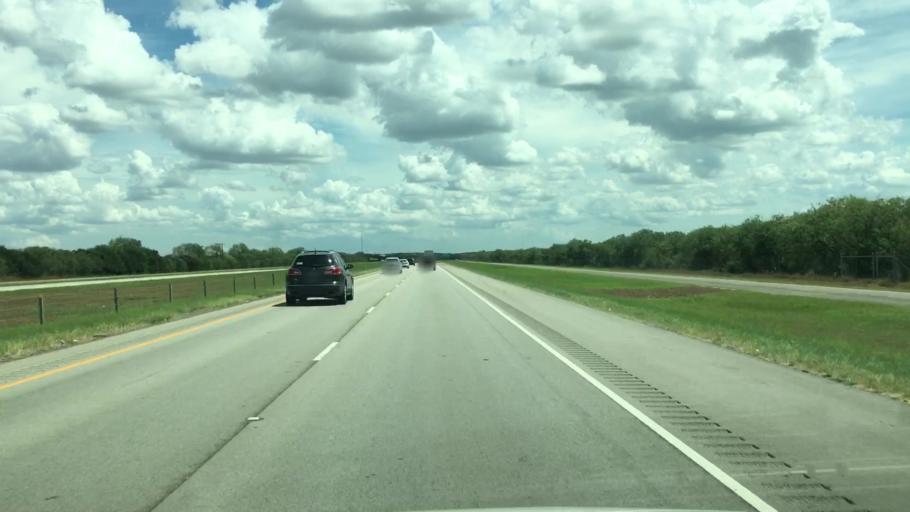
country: US
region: Texas
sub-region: Live Oak County
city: George West
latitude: 28.2792
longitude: -97.9542
